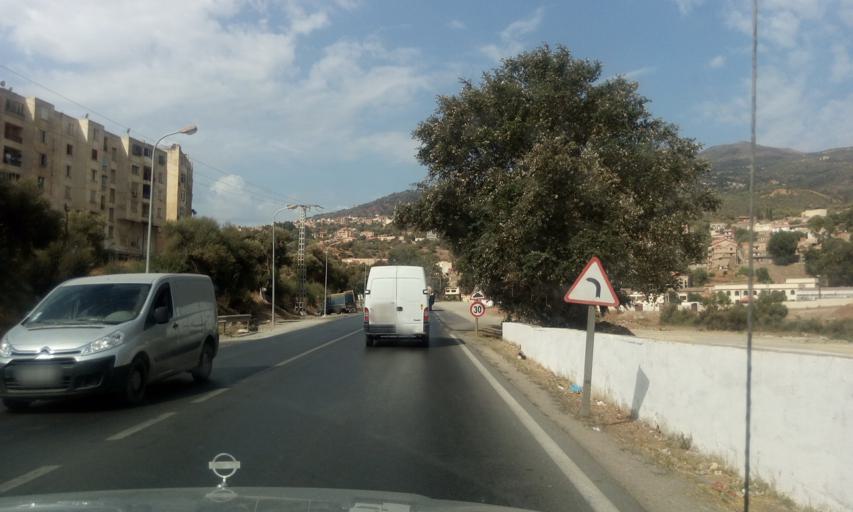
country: DZ
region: Bejaia
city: Seddouk
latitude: 36.6108
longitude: 4.6881
